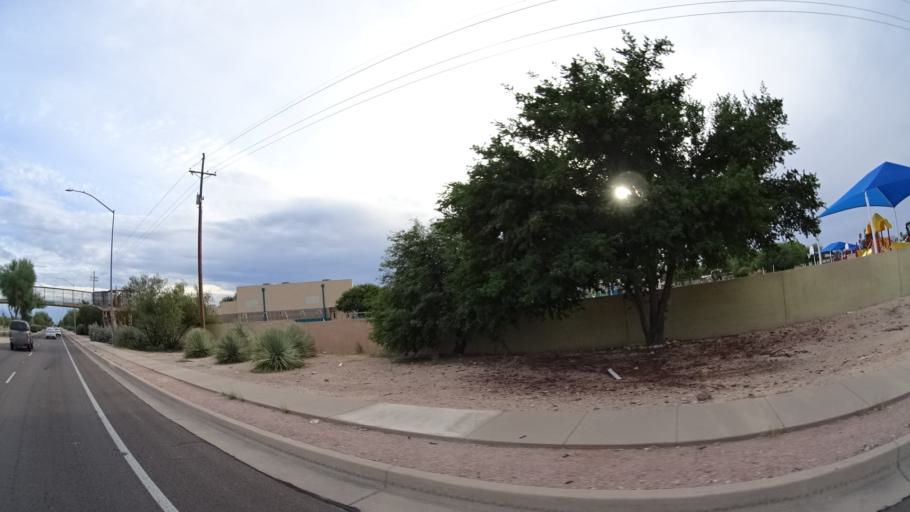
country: US
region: Arizona
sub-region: Pima County
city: South Tucson
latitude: 32.1563
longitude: -110.9351
